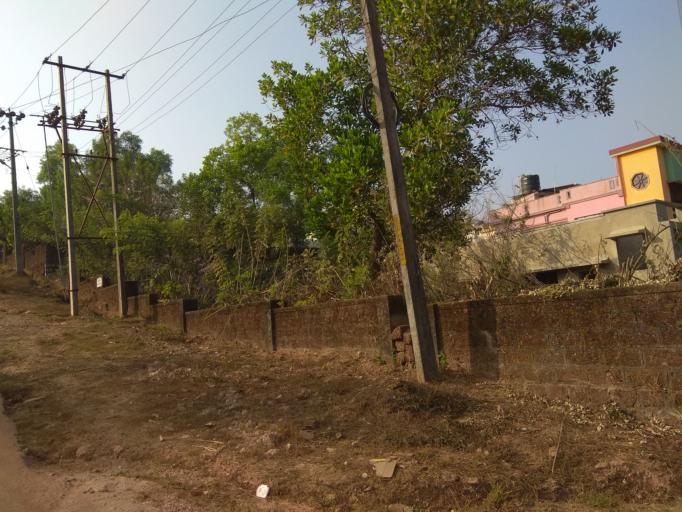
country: IN
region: Karnataka
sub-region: Dakshina Kannada
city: Mangalore
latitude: 12.9231
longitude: 74.8715
